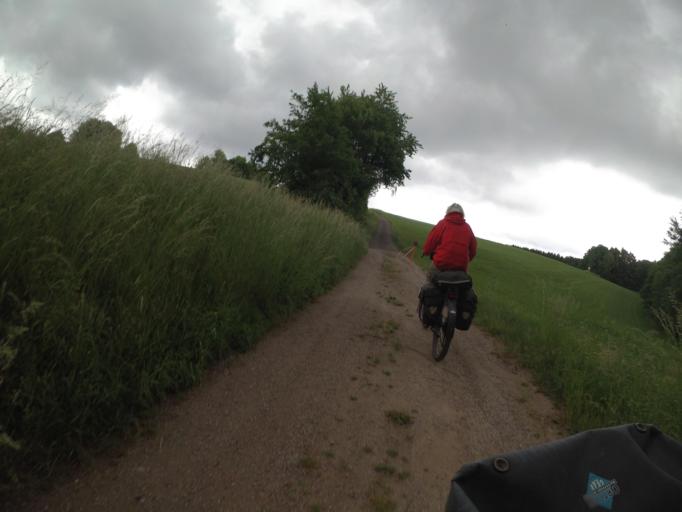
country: DE
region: Rheinland-Pfalz
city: Obersimten
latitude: 49.1685
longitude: 7.5988
